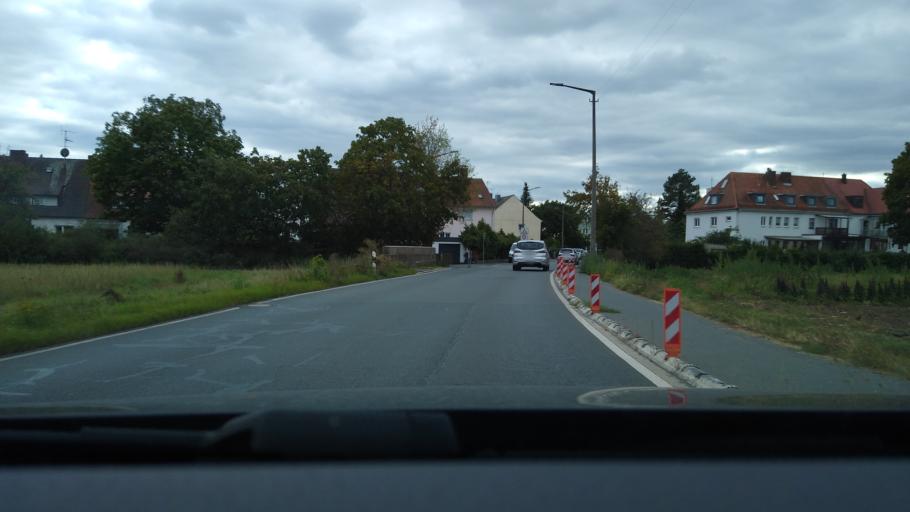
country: DE
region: Bavaria
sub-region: Regierungsbezirk Mittelfranken
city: Wetzendorf
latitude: 49.4715
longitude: 11.0304
